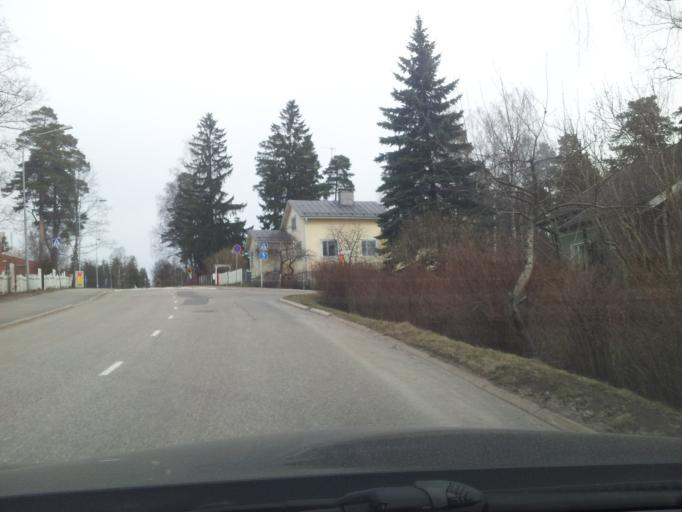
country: FI
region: Uusimaa
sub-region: Helsinki
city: Kilo
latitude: 60.2027
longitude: 24.8053
